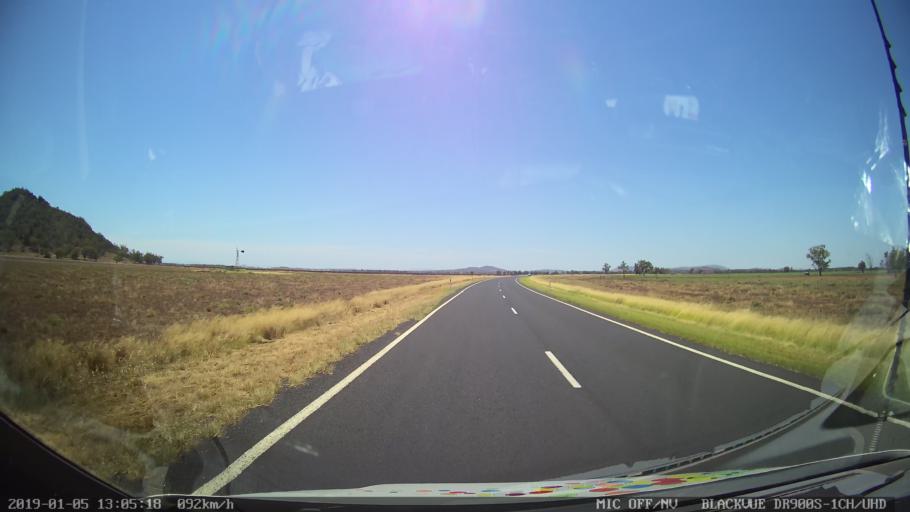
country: AU
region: New South Wales
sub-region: Gunnedah
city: Gunnedah
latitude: -31.0965
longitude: 149.8512
